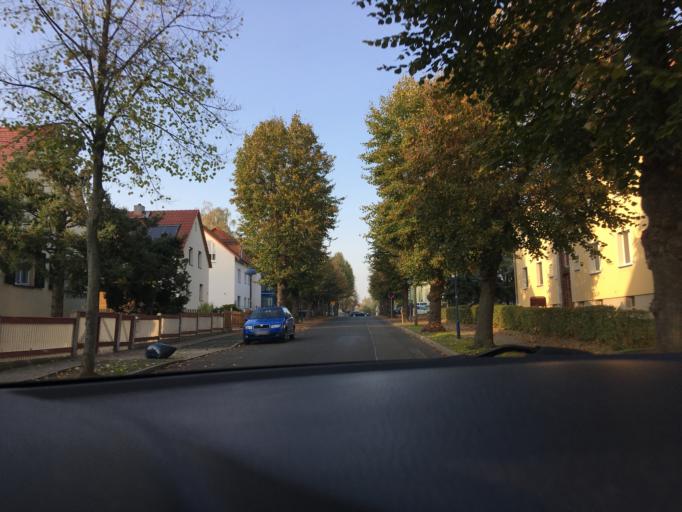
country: DE
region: Saxony
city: Rotha
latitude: 51.1977
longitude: 12.4172
